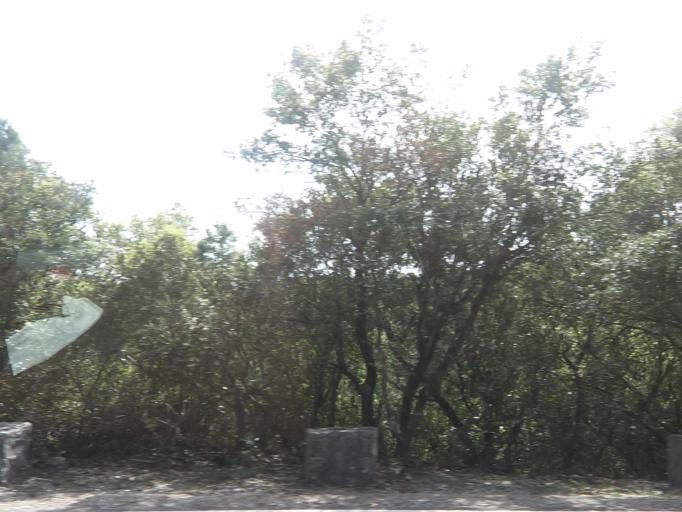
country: PT
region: Setubal
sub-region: Sesimbra
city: Sesimbra
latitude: 38.4611
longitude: -9.0081
